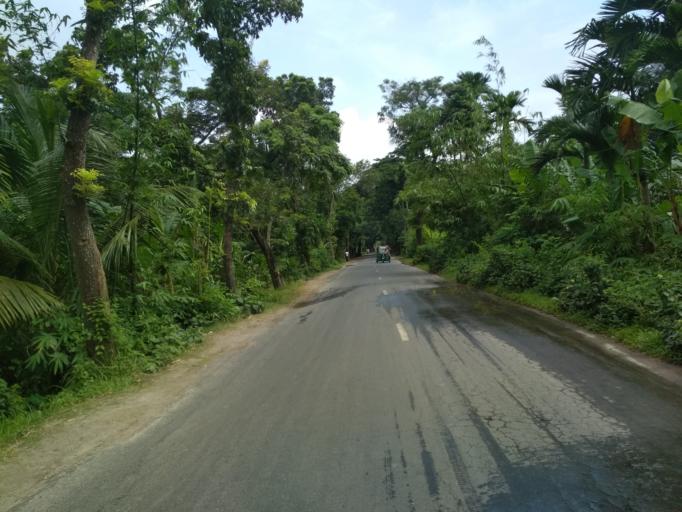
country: BD
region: Chittagong
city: Lakshmipur
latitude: 22.9546
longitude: 90.8090
